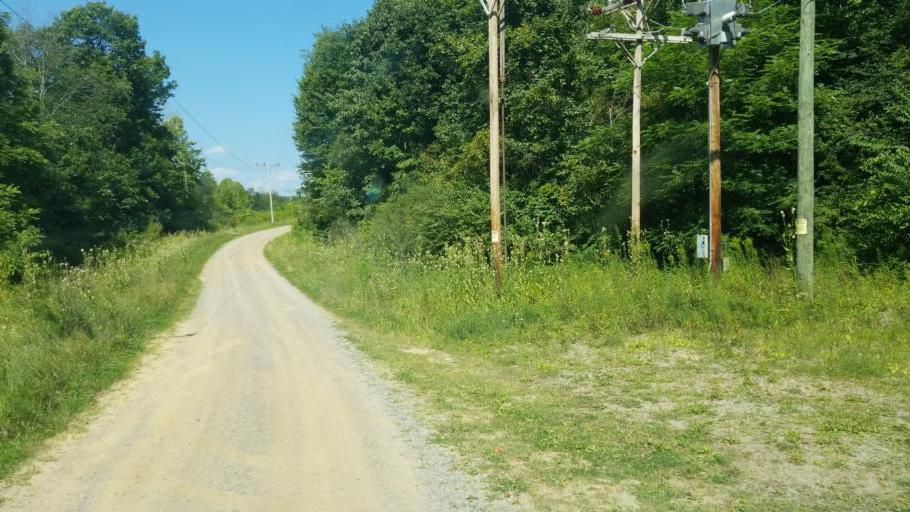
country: US
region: Pennsylvania
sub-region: Clarion County
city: Knox
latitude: 41.1098
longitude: -79.5399
